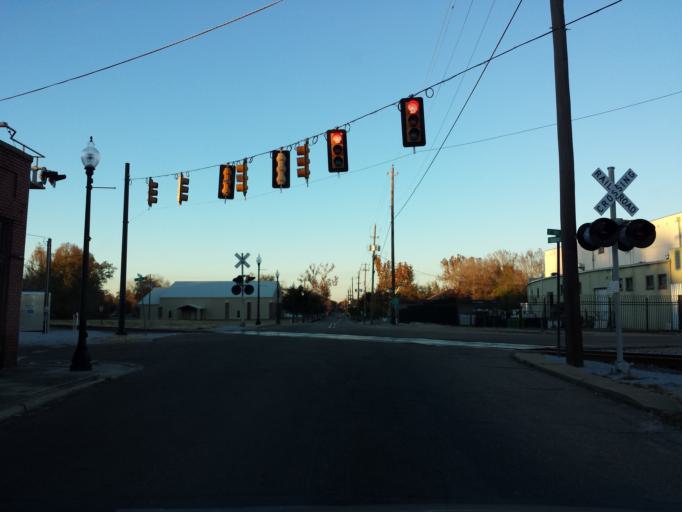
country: US
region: Mississippi
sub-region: Forrest County
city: Hattiesburg
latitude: 31.3297
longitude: -89.2900
